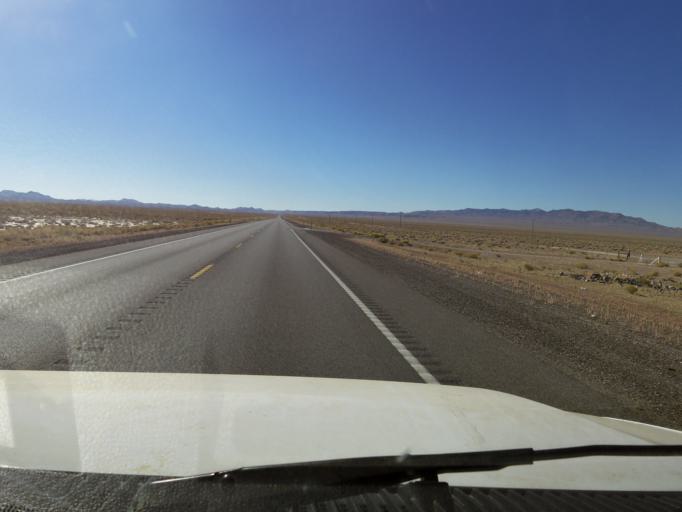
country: US
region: Nevada
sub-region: Esmeralda County
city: Goldfield
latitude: 37.8752
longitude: -117.2422
